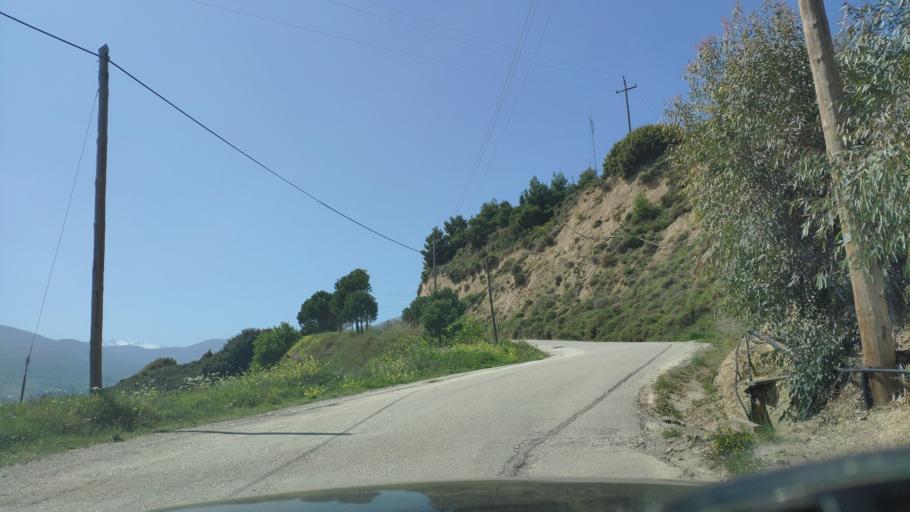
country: GR
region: West Greece
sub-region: Nomos Achaias
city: Aiyira
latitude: 38.1173
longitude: 22.3335
